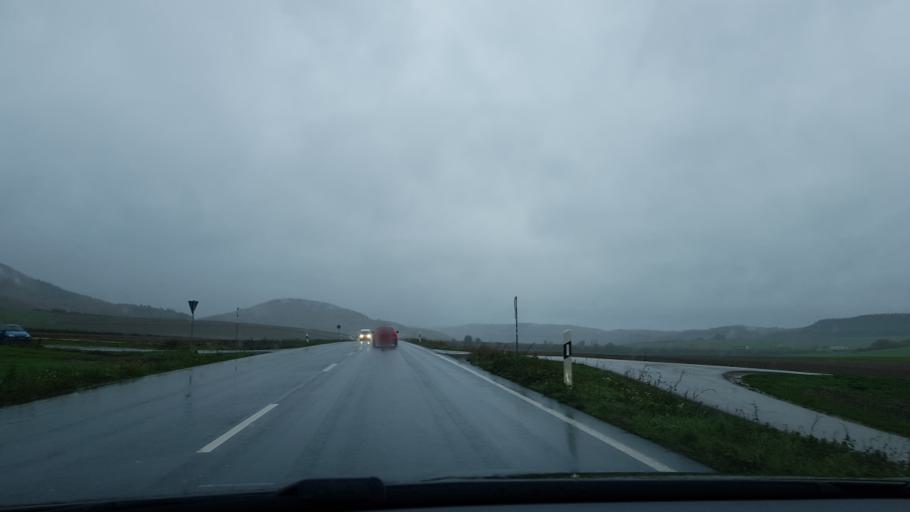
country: DE
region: Rheinland-Pfalz
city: Salmtal
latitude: 49.9647
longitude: 6.8564
